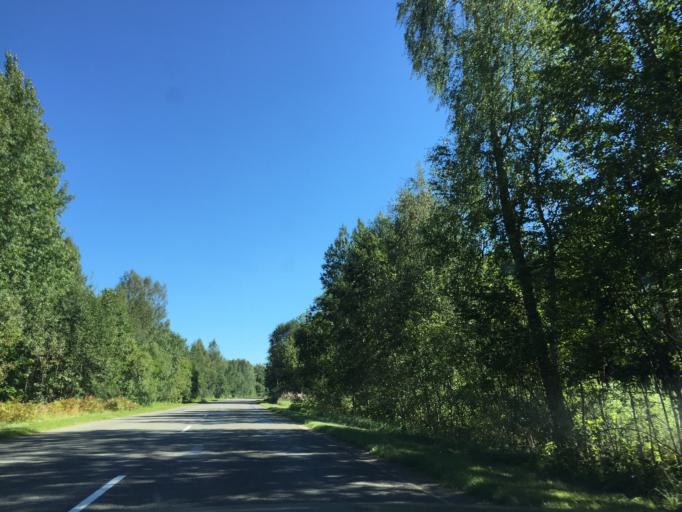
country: LV
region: Akniste
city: Akniste
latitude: 56.1394
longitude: 25.8142
